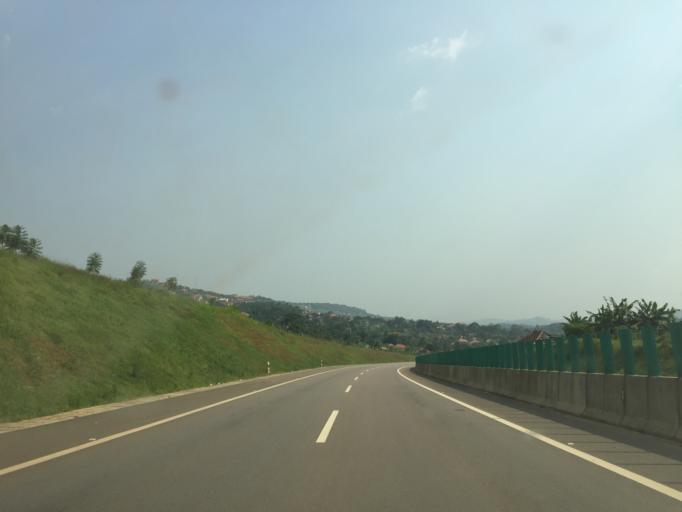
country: UG
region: Central Region
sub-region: Wakiso District
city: Kajansi
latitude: 0.2591
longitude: 32.5217
